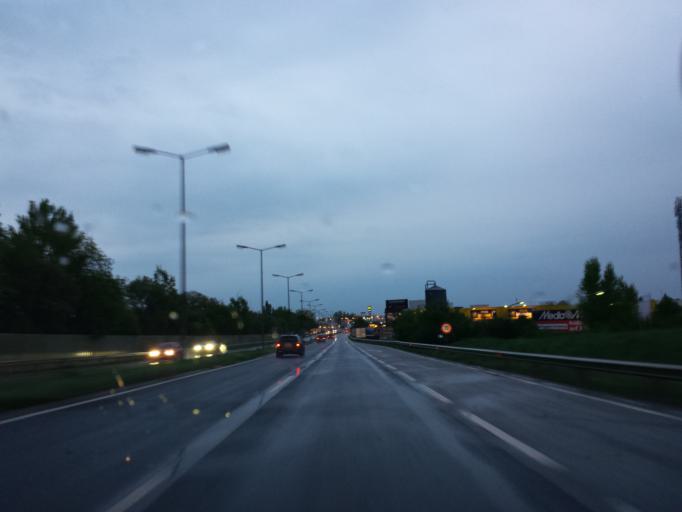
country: AT
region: Lower Austria
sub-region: Politischer Bezirk Modling
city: Brunn am Gebirge
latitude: 48.1157
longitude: 16.3000
